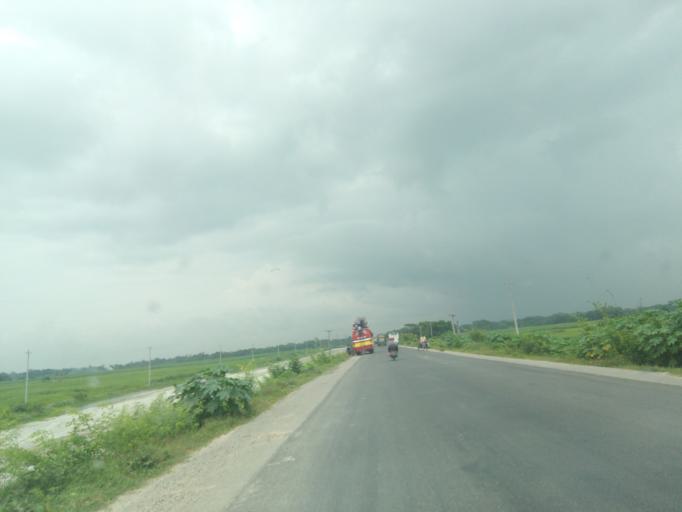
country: BD
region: Dhaka
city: Char Bhadrasan
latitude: 23.3700
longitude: 90.0507
